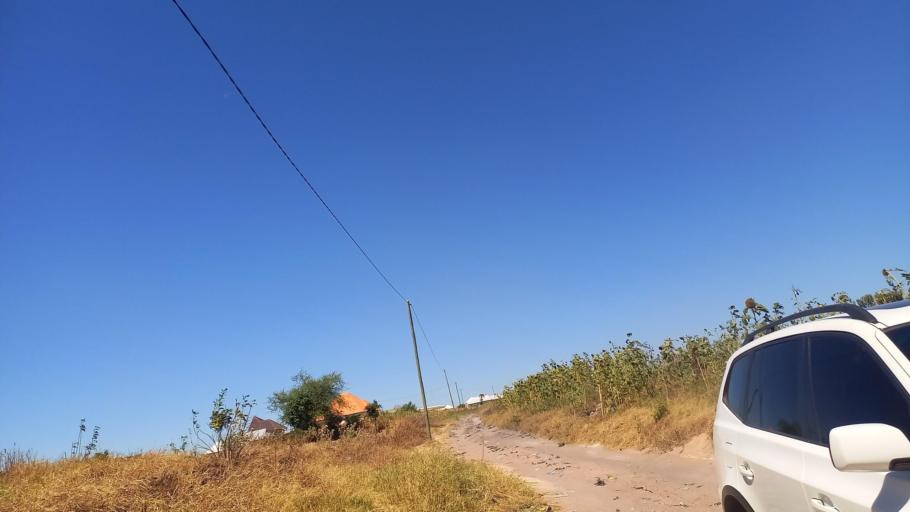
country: TZ
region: Dodoma
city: Dodoma
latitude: -6.1332
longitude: 35.6962
